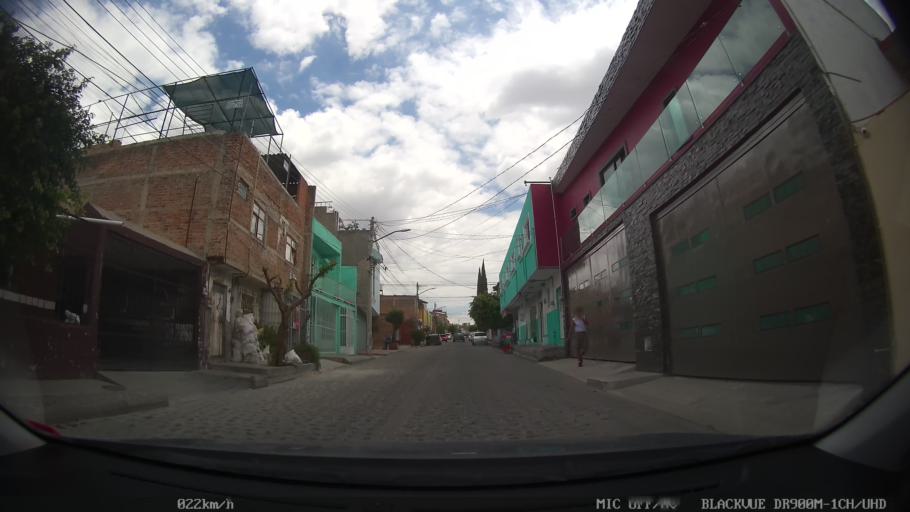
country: MX
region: Jalisco
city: Tlaquepaque
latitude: 20.6370
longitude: -103.2699
